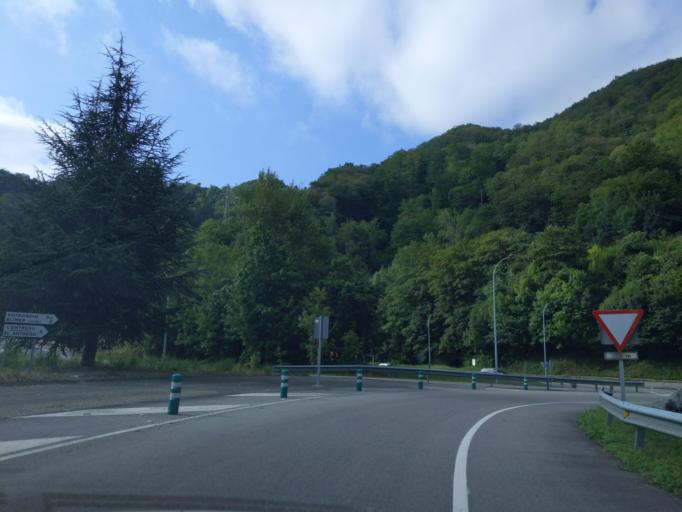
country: ES
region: Asturias
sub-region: Province of Asturias
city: El entrego
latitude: 43.2737
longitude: -5.6142
